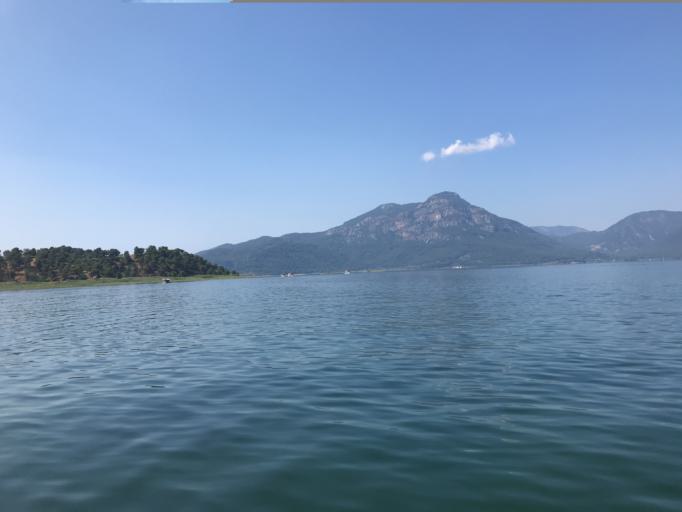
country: TR
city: Dalyan
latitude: 36.9024
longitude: 28.6465
